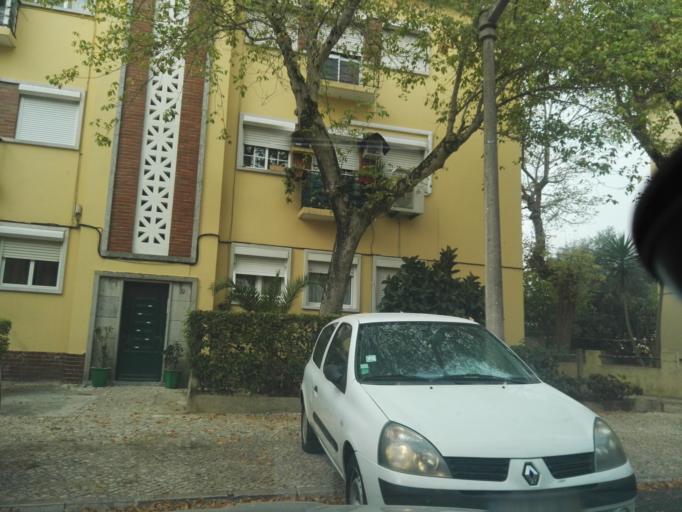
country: PT
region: Lisbon
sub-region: Lisbon
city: Lisbon
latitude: 38.7530
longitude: -9.1473
